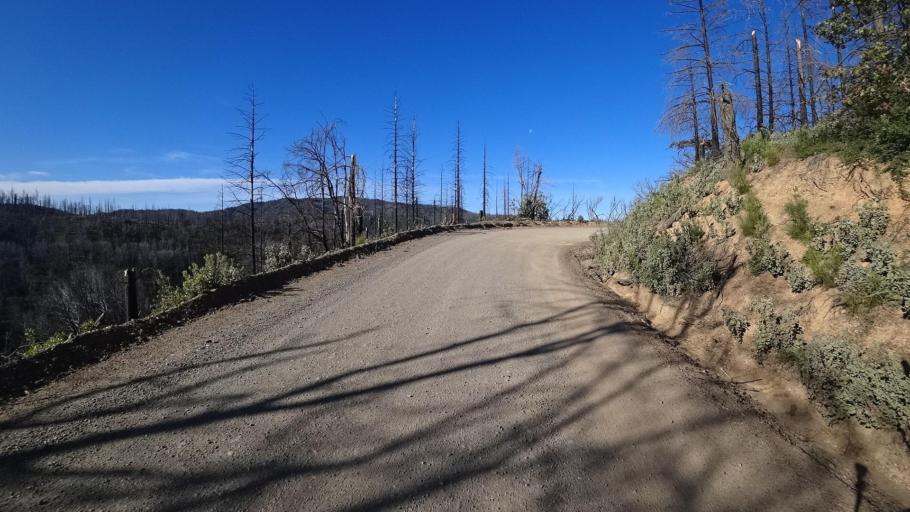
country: US
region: California
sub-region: Lake County
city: Upper Lake
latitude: 39.3453
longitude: -122.9653
